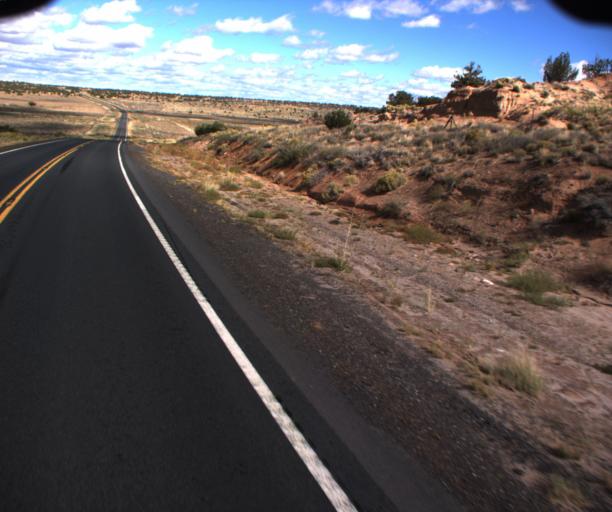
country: US
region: Arizona
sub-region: Apache County
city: Houck
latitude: 35.0890
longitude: -109.3110
